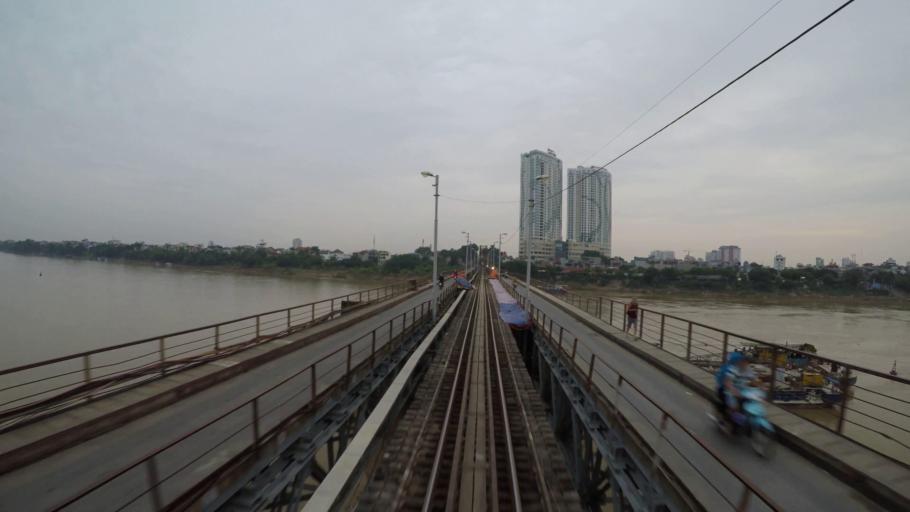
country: VN
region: Ha Noi
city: Hoan Kiem
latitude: 21.0541
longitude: 105.8863
